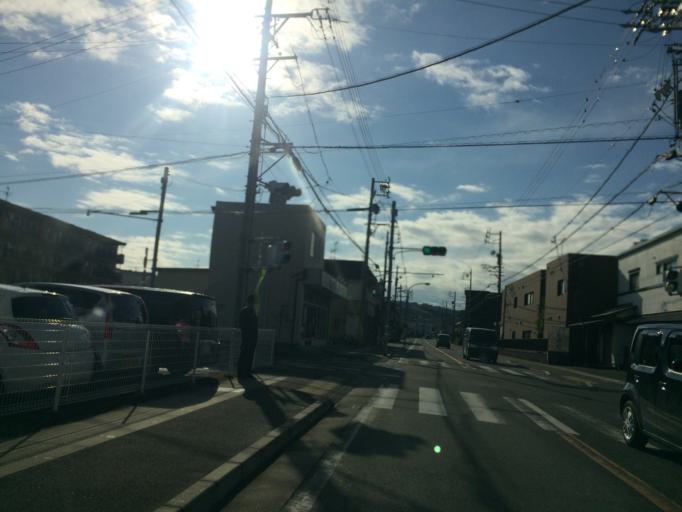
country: JP
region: Shizuoka
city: Shizuoka-shi
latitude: 34.9868
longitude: 138.4249
